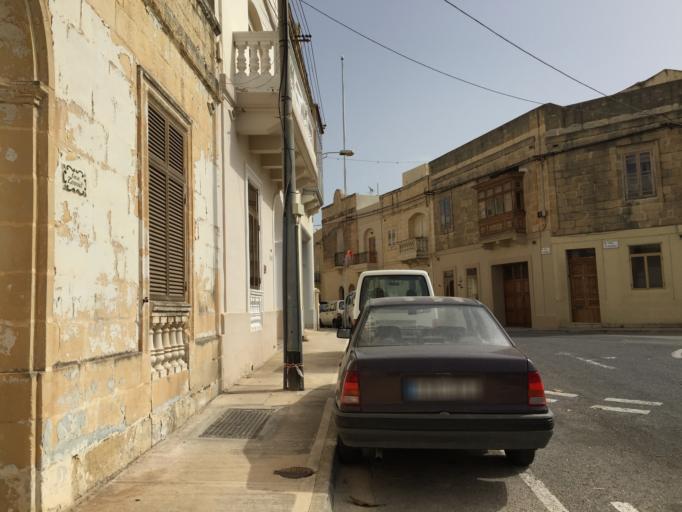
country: MT
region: Bormla
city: Cospicua
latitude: 35.8911
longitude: 14.5268
